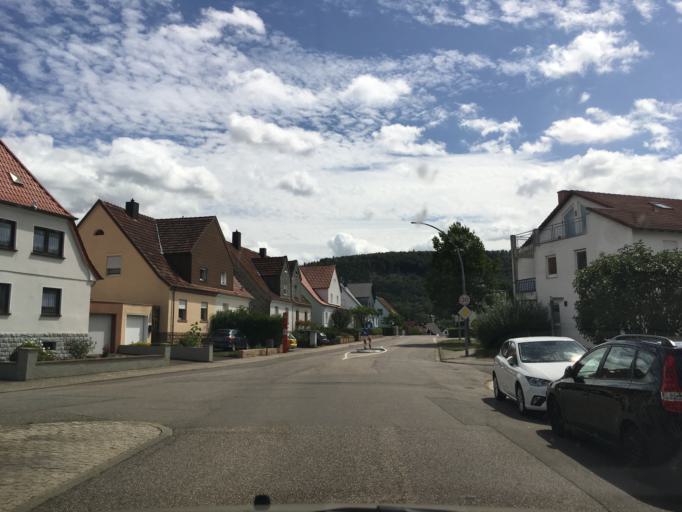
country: DE
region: Saarland
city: Sankt Ingbert
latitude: 49.2719
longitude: 7.1211
